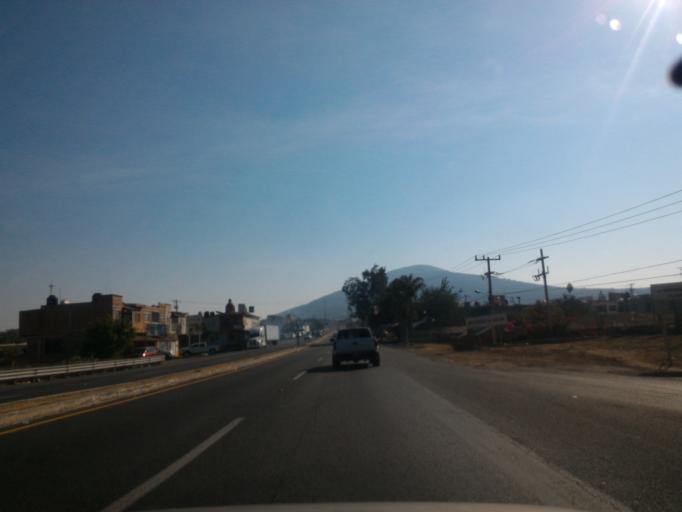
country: MX
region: Jalisco
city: Atotonilquillo
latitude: 20.3911
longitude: -103.1224
